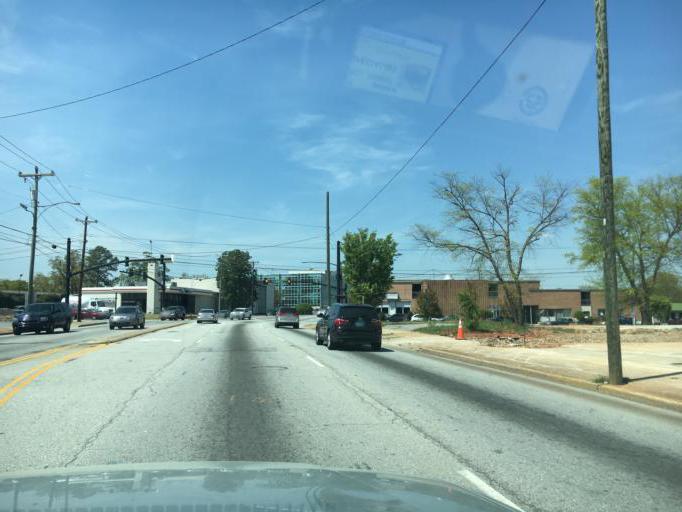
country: US
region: South Carolina
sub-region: Spartanburg County
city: Spartanburg
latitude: 34.9516
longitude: -81.9201
